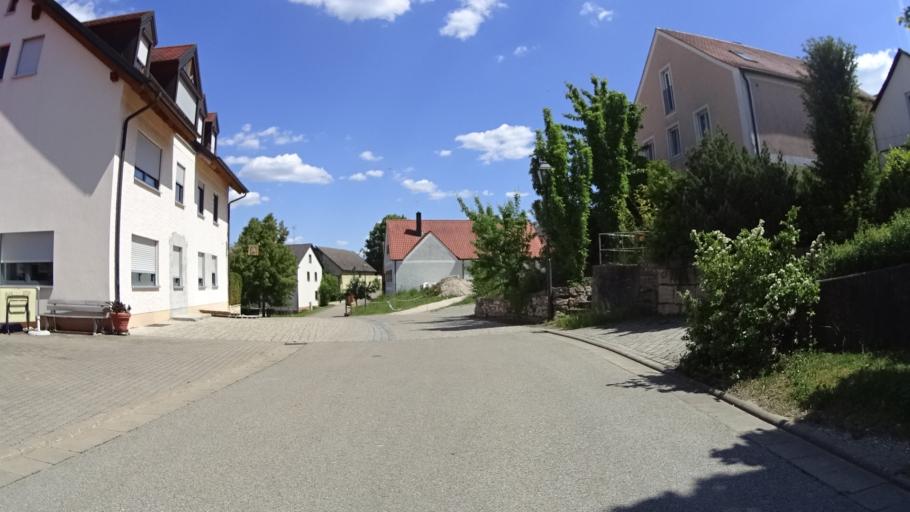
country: DE
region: Bavaria
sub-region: Regierungsbezirk Mittelfranken
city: Greding
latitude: 49.0716
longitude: 11.2919
